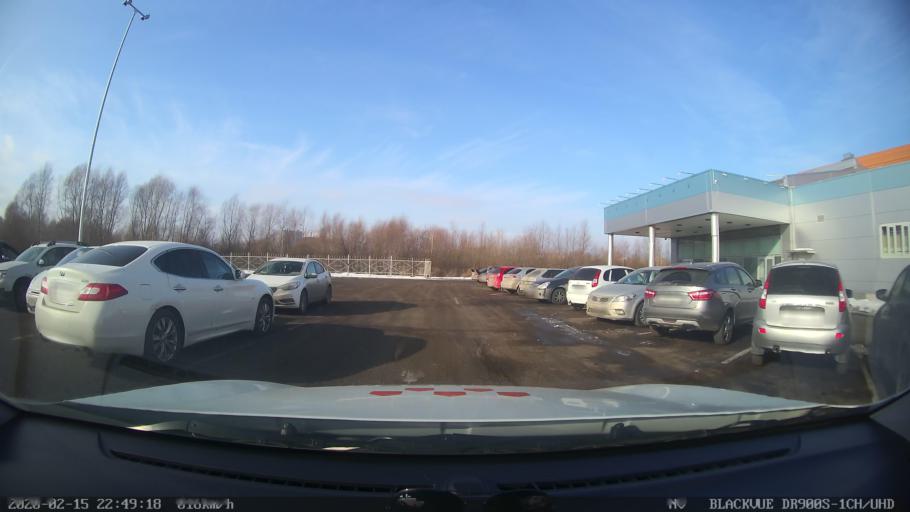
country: RU
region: Tatarstan
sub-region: Gorod Kazan'
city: Kazan
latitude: 55.8299
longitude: 49.1159
